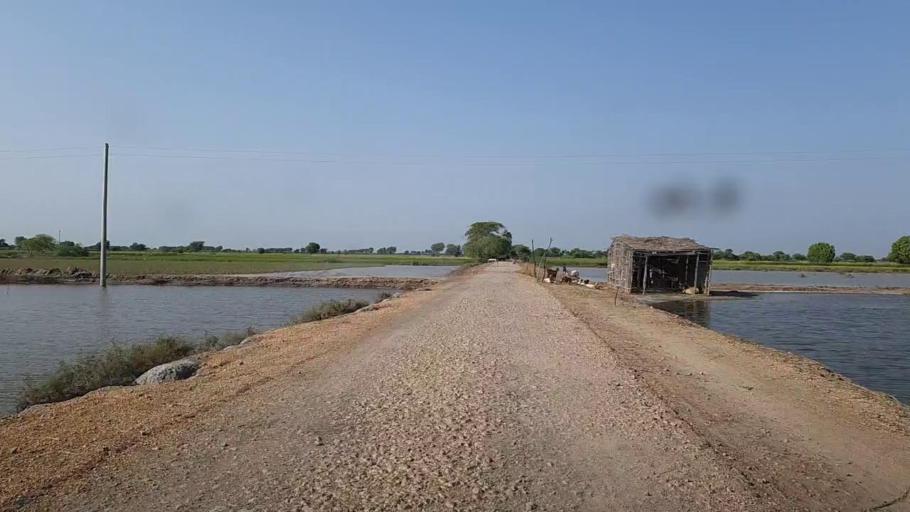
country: PK
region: Sindh
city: Bulri
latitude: 24.7765
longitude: 68.4335
